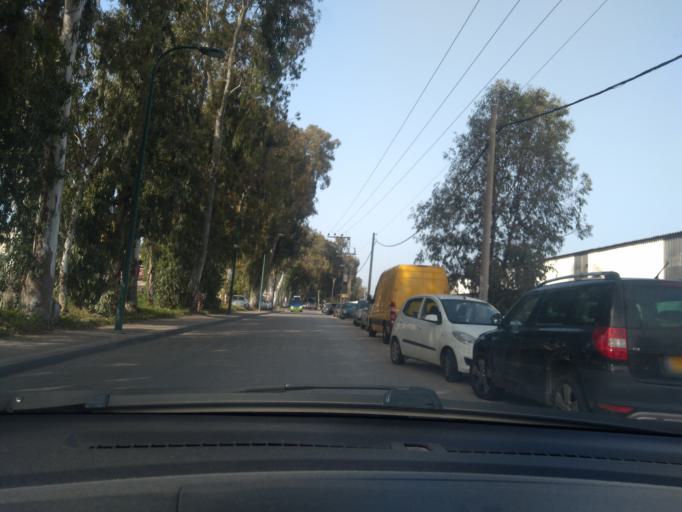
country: IL
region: Central District
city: Netanya
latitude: 32.3208
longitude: 34.8682
